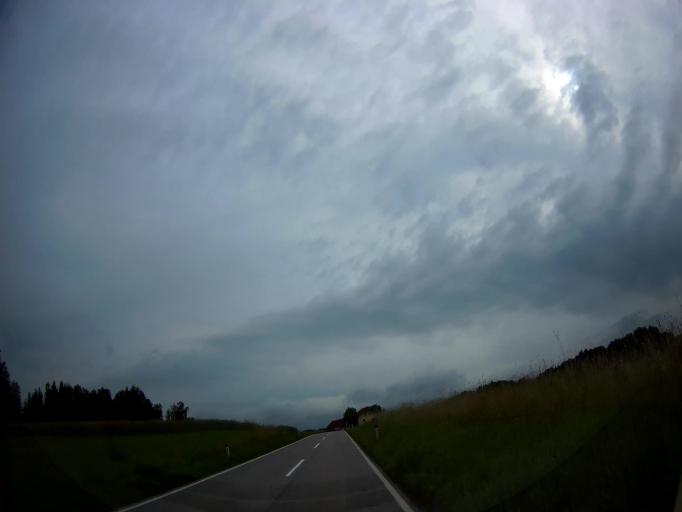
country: AT
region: Salzburg
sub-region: Politischer Bezirk Salzburg-Umgebung
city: Mattsee
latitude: 48.0185
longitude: 13.1292
